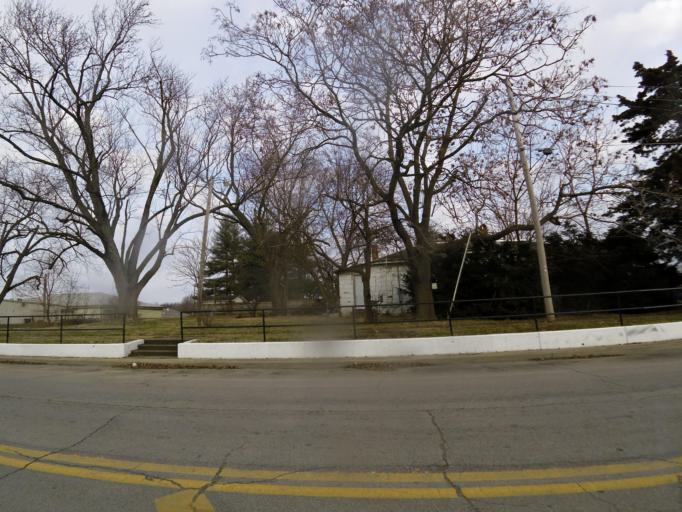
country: US
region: Illinois
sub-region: Christian County
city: Pana
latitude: 39.3891
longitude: -89.0729
